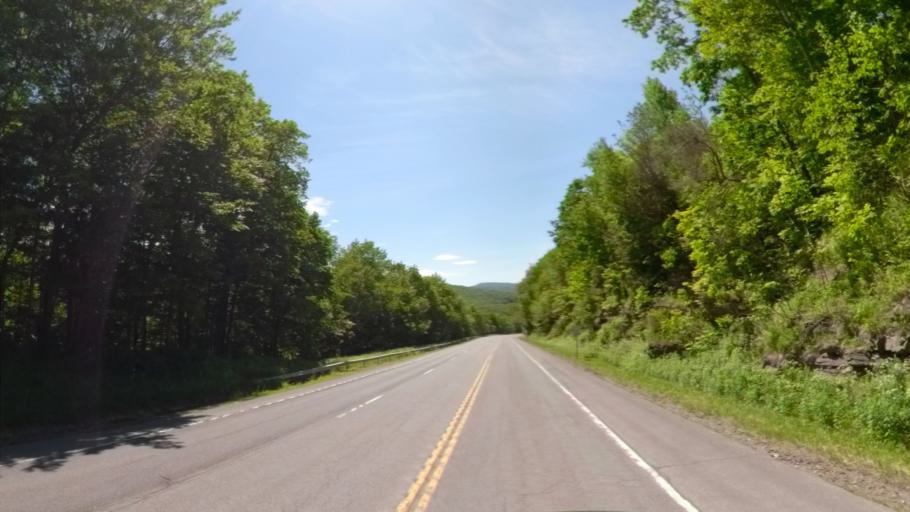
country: US
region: New York
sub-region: Delaware County
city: Stamford
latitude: 42.1410
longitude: -74.4859
